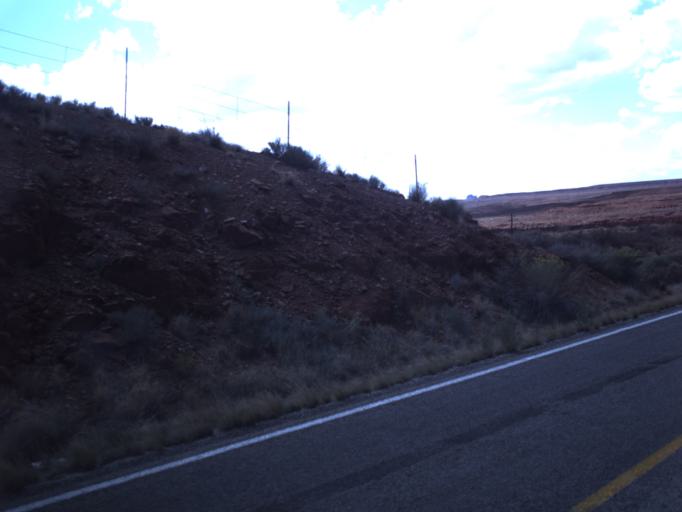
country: US
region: Utah
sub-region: San Juan County
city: Blanding
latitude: 37.2152
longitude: -109.8394
